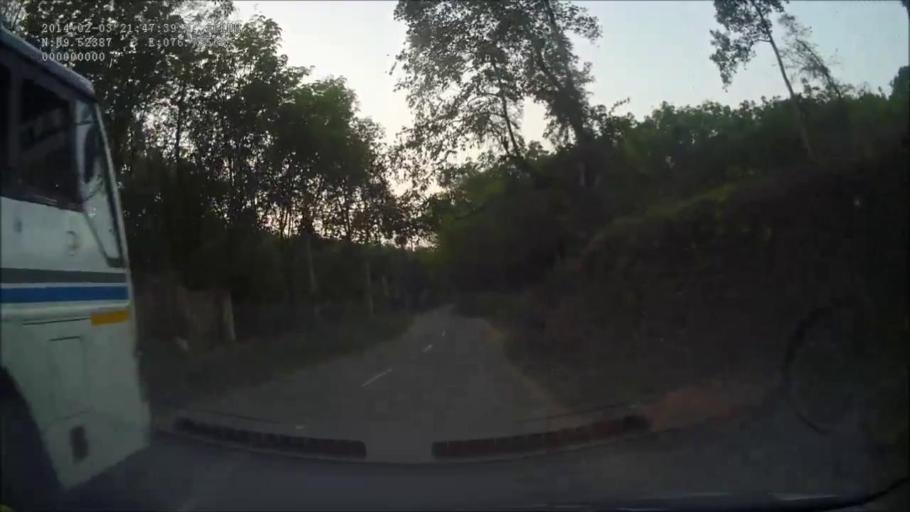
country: IN
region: Kerala
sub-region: Kottayam
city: Erattupetta
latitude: 9.5246
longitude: 76.7337
